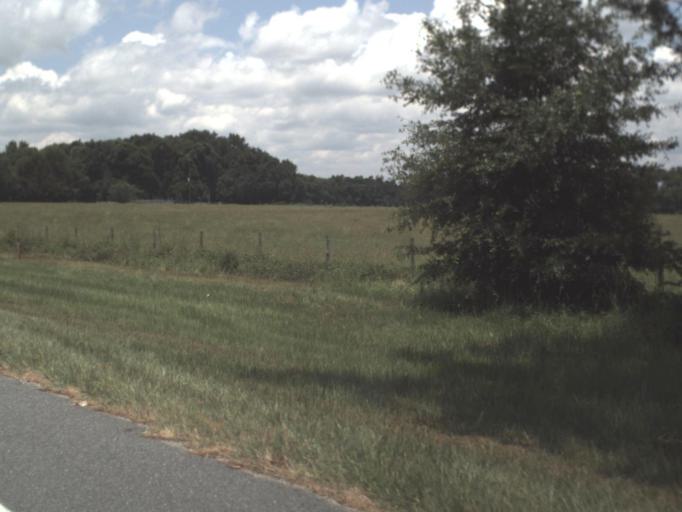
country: US
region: Florida
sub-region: Alachua County
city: High Springs
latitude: 30.0043
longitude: -82.5661
